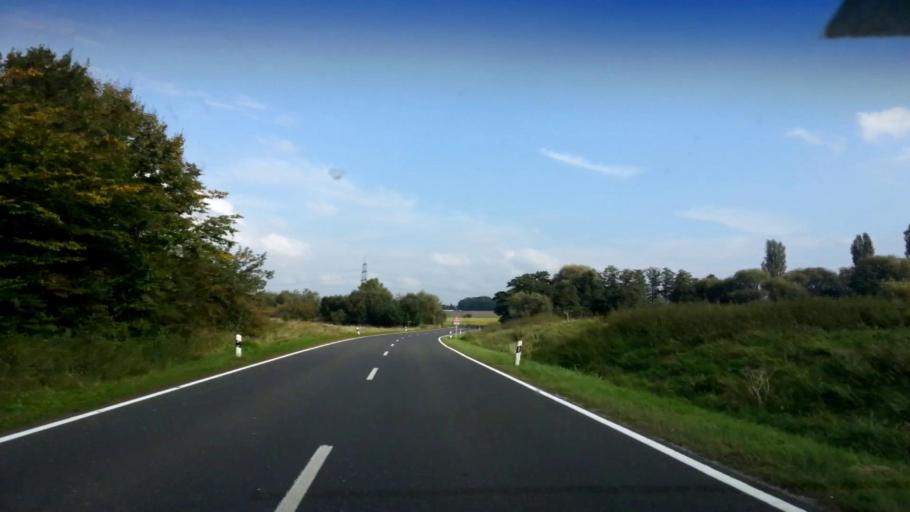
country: DE
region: Bavaria
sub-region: Regierungsbezirk Unterfranken
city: Wiesenbronn
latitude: 49.7560
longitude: 10.3242
